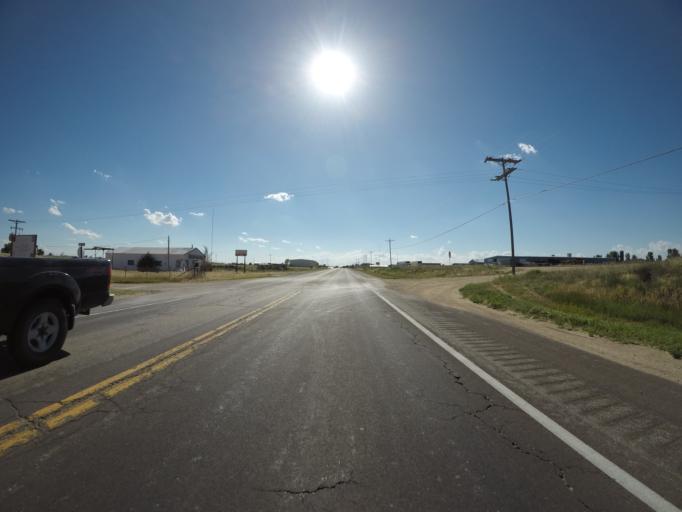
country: US
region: Colorado
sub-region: Logan County
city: Sterling
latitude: 40.6238
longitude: -103.2828
